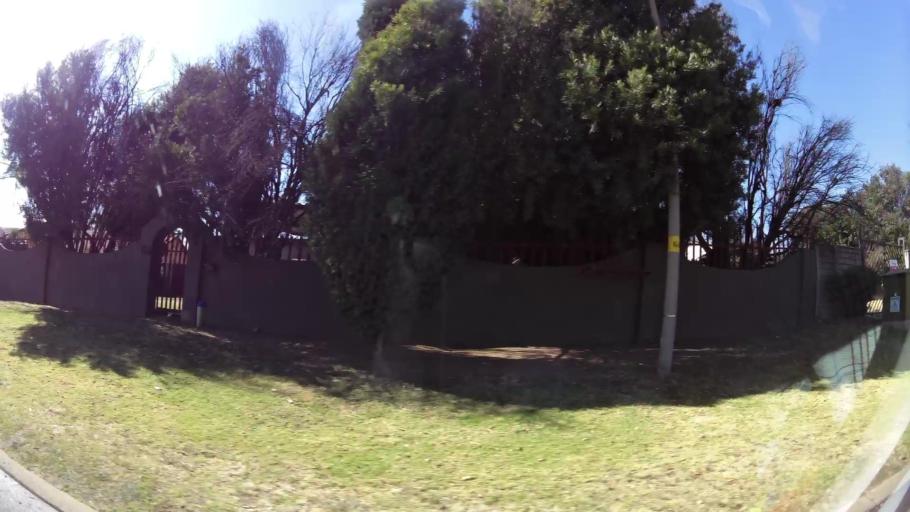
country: ZA
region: Gauteng
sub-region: City of Johannesburg Metropolitan Municipality
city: Modderfontein
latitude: -26.0565
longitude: 28.2142
